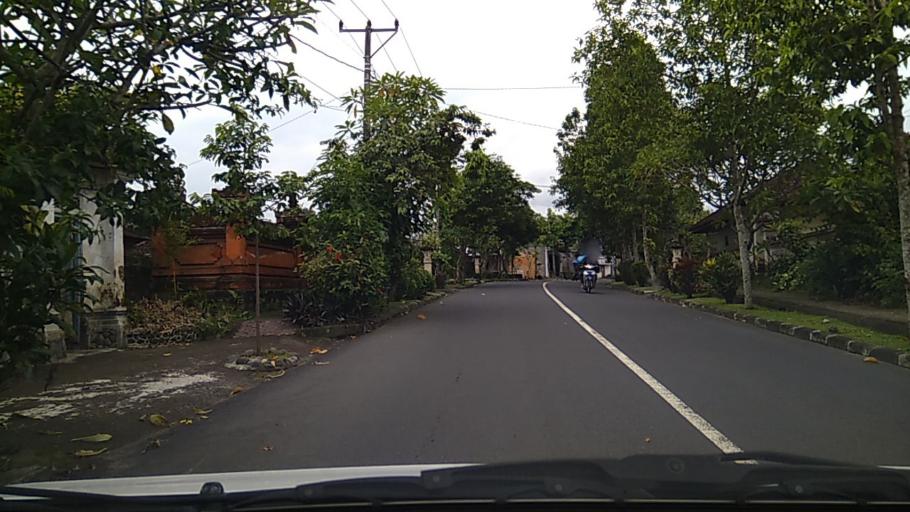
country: ID
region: Bali
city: Banjar Kelodan
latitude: -8.5211
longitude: 115.3456
